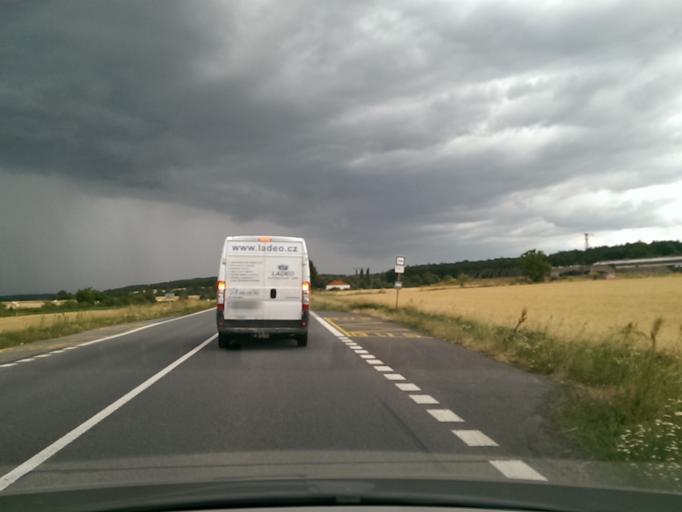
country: CZ
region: Central Bohemia
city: Loucen
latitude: 50.2518
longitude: 14.9949
